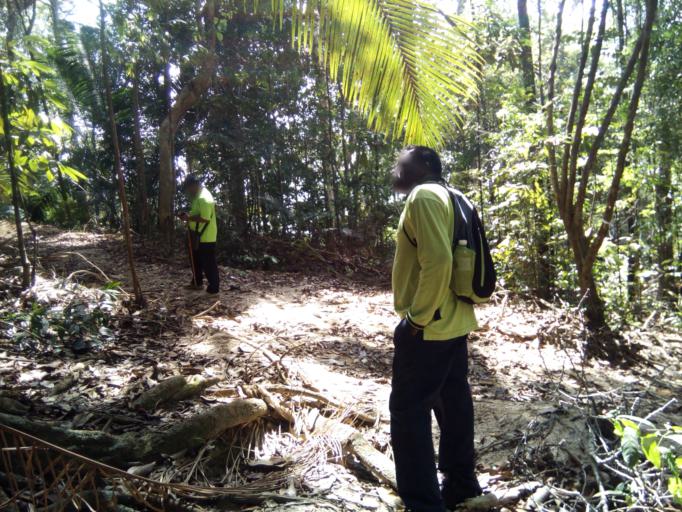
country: MY
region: Penang
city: Tanjung Tokong
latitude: 5.4436
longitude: 100.2900
